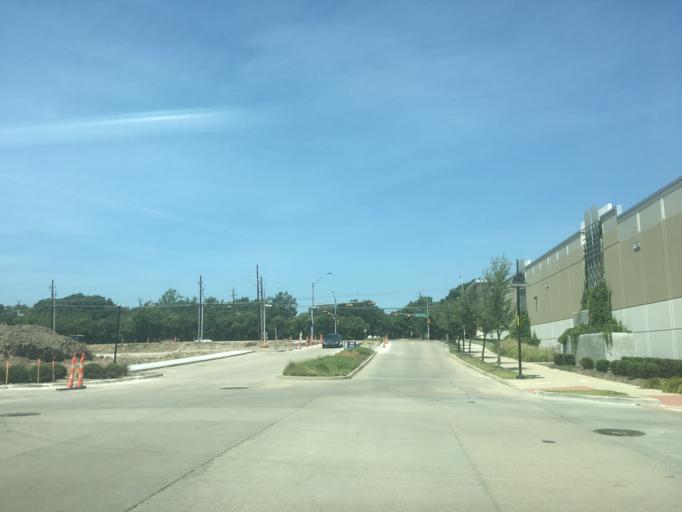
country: US
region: Texas
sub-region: Dallas County
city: University Park
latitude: 32.8758
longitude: -96.7334
